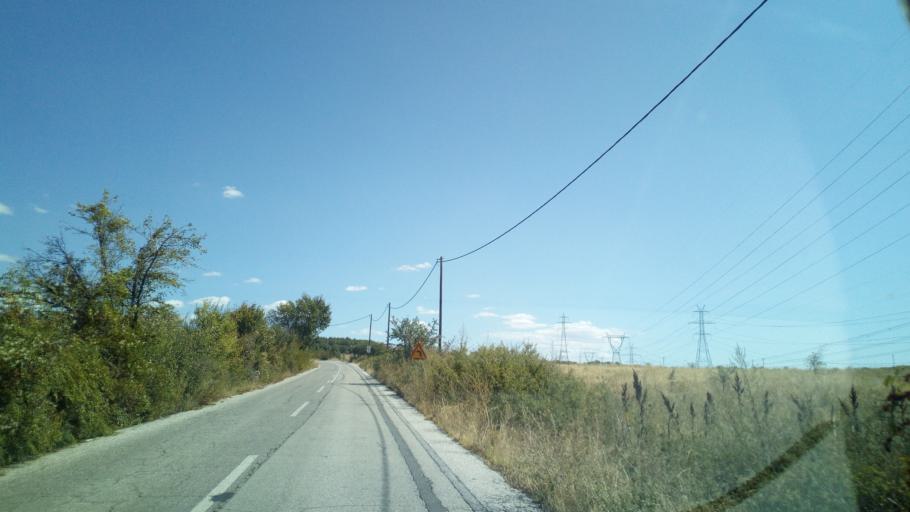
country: GR
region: Central Macedonia
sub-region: Nomos Thessalonikis
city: Kolchikon
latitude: 40.8018
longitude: 23.1488
